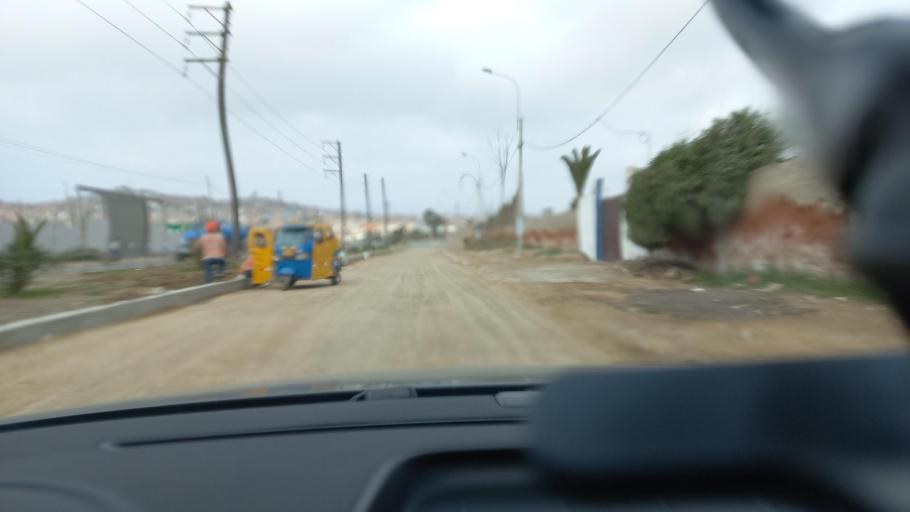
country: PE
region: Lima
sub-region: Lima
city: Surco
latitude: -12.2048
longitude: -77.0007
